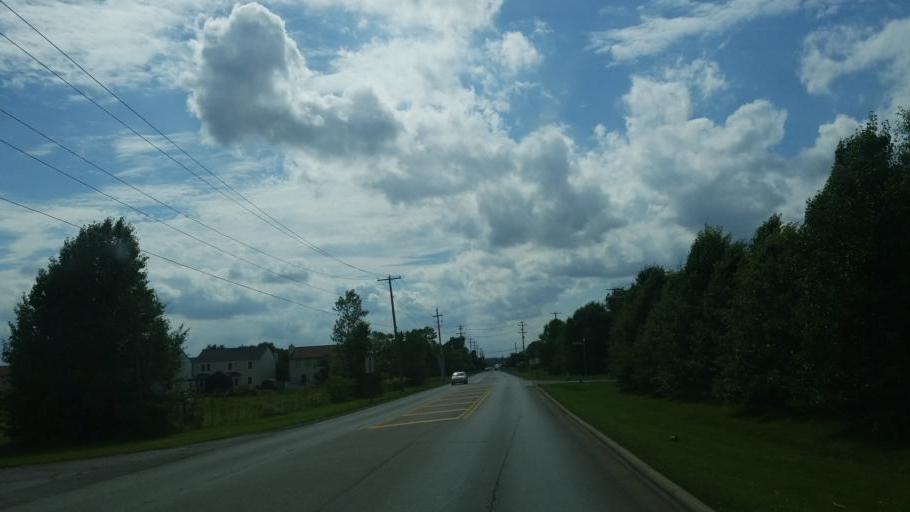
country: US
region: Ohio
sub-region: Franklin County
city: Reynoldsburg
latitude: 39.9264
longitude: -82.8095
